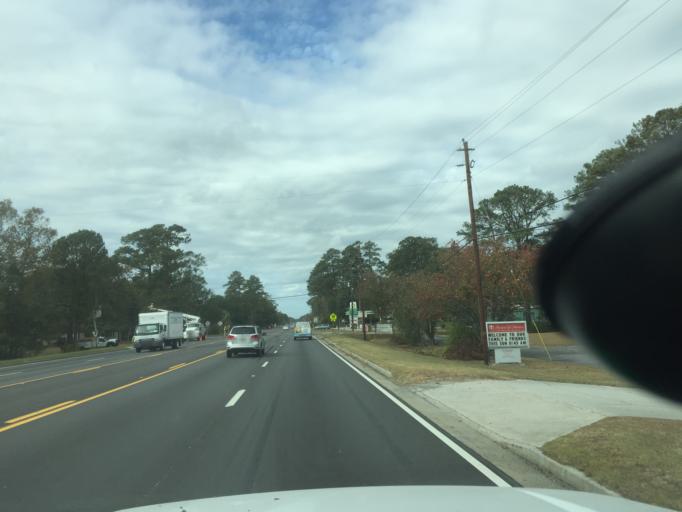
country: US
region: Georgia
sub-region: Chatham County
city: Garden City
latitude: 32.0881
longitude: -81.1758
